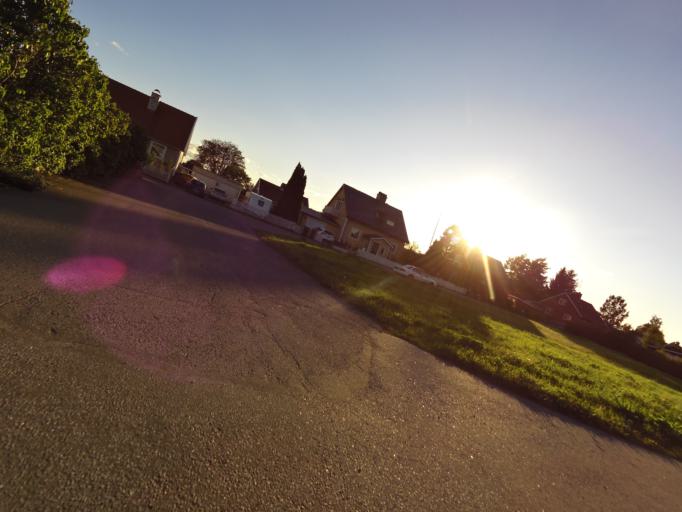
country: SE
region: Gaevleborg
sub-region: Gavle Kommun
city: Gavle
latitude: 60.7169
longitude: 17.1661
